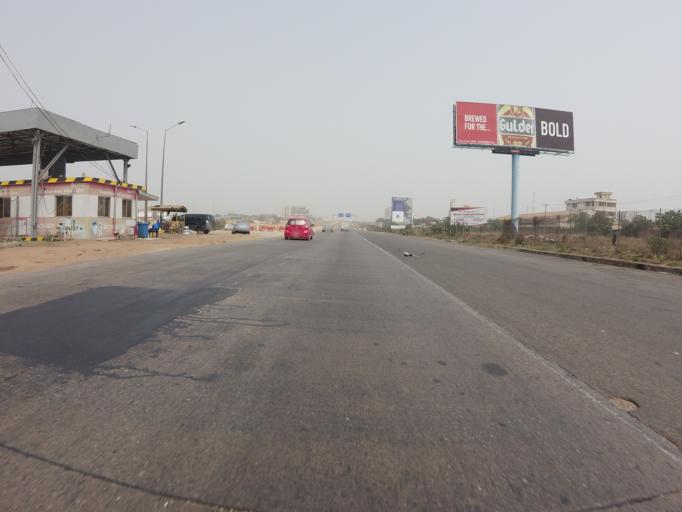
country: GH
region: Greater Accra
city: Tema
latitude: 5.6834
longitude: -0.0228
